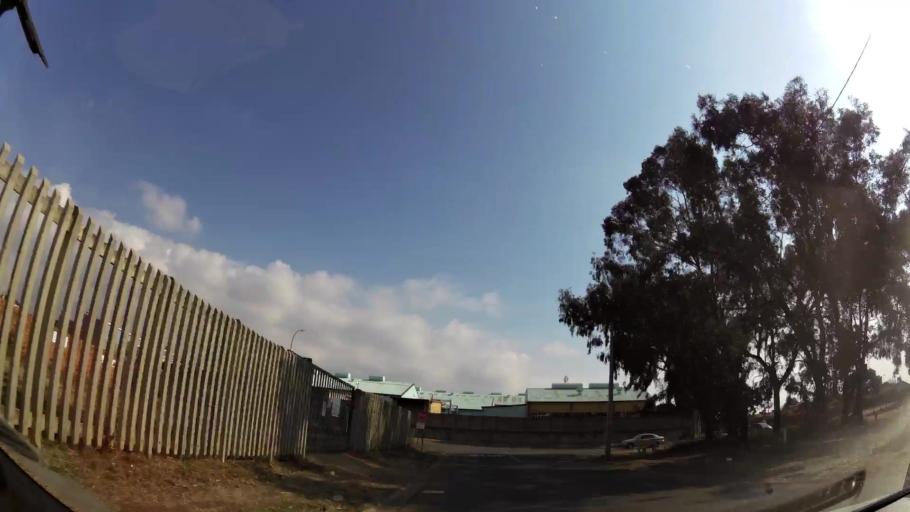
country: ZA
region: Gauteng
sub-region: Ekurhuleni Metropolitan Municipality
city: Germiston
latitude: -26.1644
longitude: 28.2009
